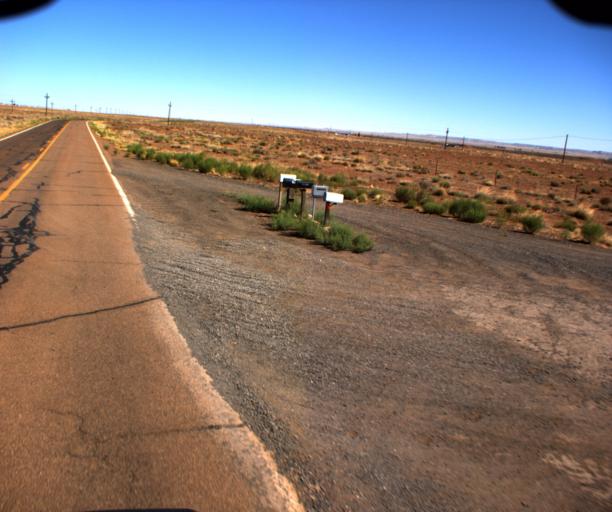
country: US
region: Arizona
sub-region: Coconino County
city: LeChee
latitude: 35.2777
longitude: -110.9802
